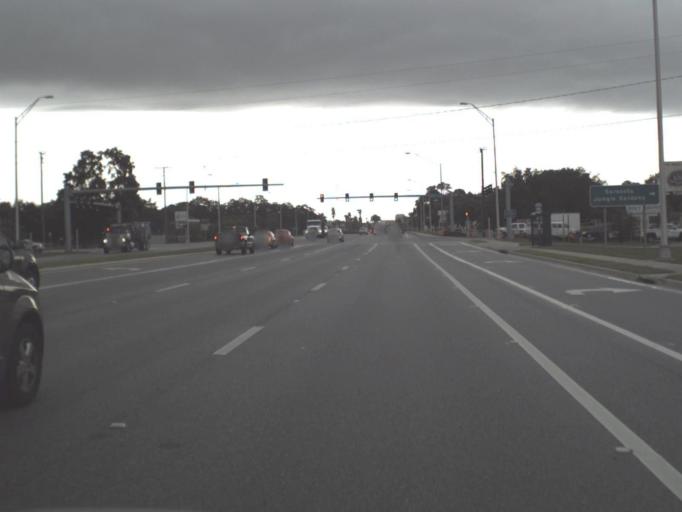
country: US
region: Florida
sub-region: Sarasota County
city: North Sarasota
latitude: 27.3682
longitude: -82.5309
